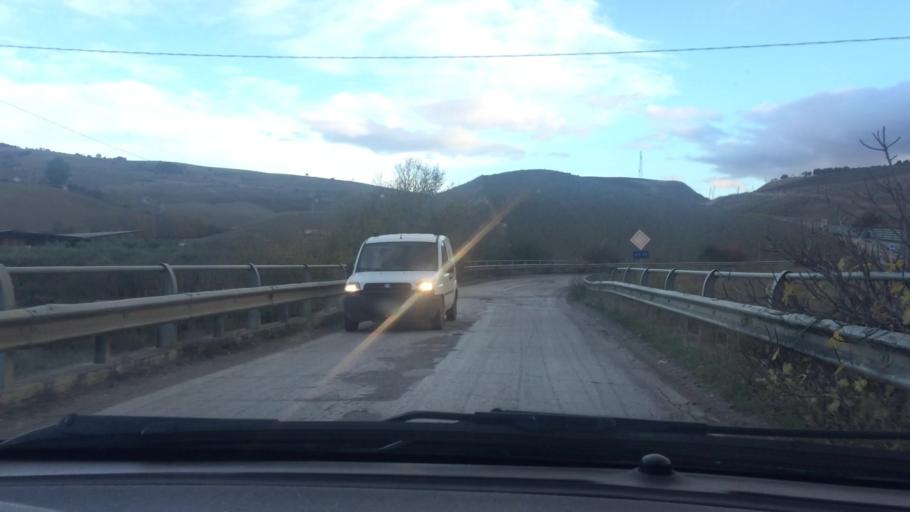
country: IT
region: Basilicate
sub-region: Provincia di Potenza
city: Tolve
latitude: 40.7025
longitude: 16.0134
